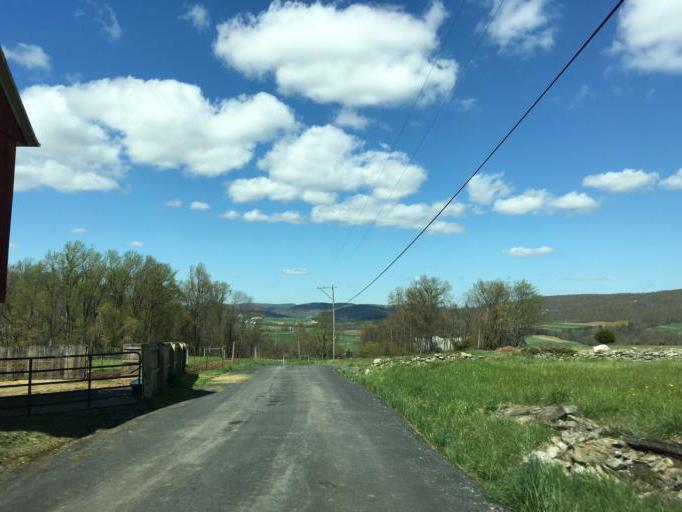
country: US
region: Maryland
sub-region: Washington County
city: Highfield-Cascade
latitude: 39.6676
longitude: -77.4715
